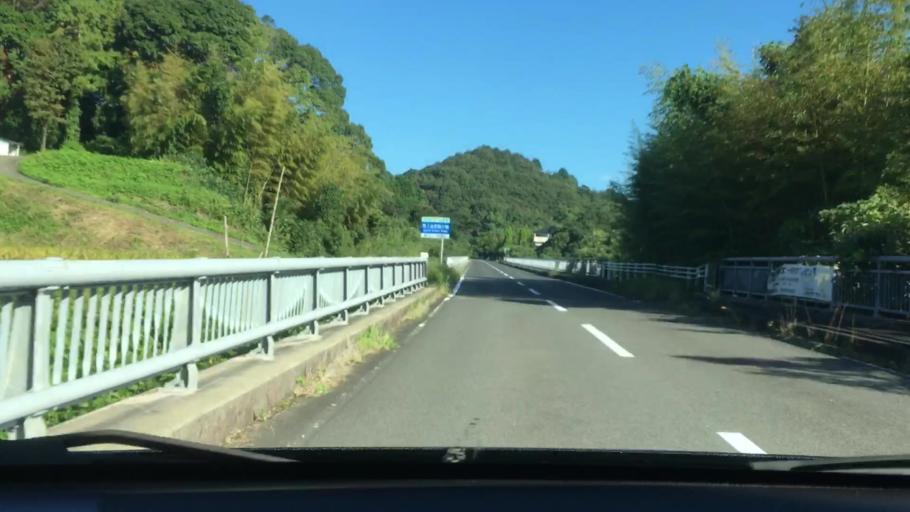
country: JP
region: Nagasaki
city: Sasebo
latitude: 32.9935
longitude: 129.7219
